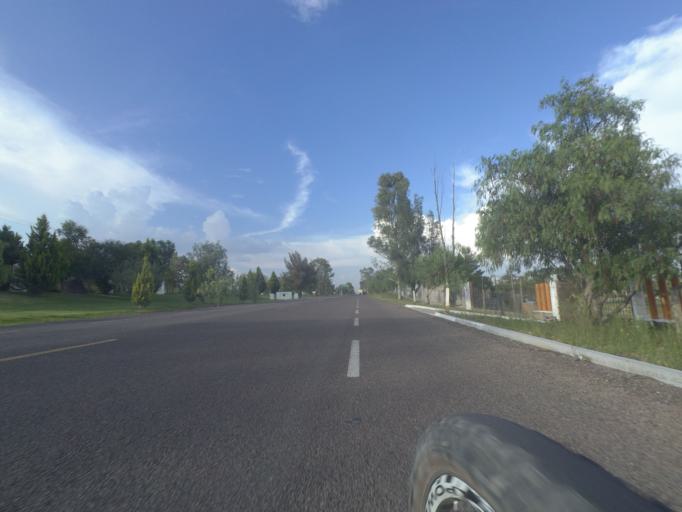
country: MX
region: Aguascalientes
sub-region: Aguascalientes
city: Penuelas (El Cienegal)
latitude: 21.7260
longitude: -102.3616
